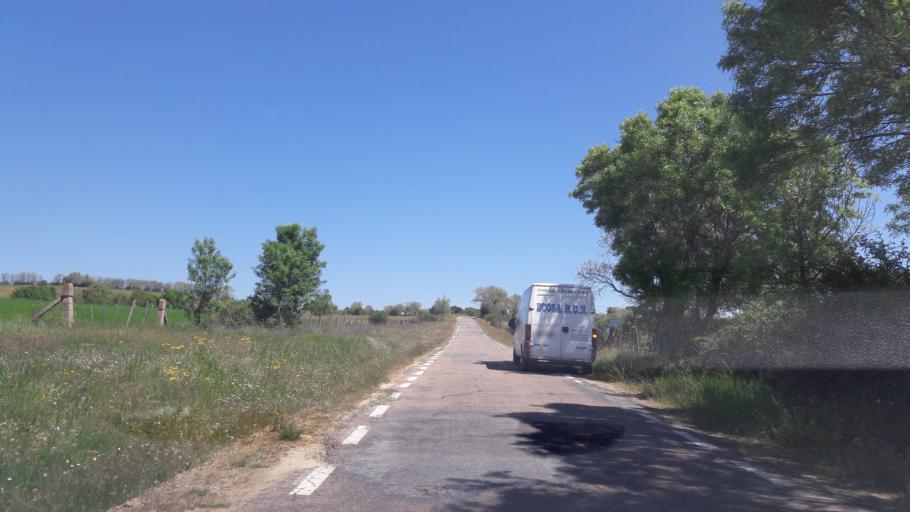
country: ES
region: Castille and Leon
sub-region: Provincia de Salamanca
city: Endrinal
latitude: 40.5684
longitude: -5.8078
